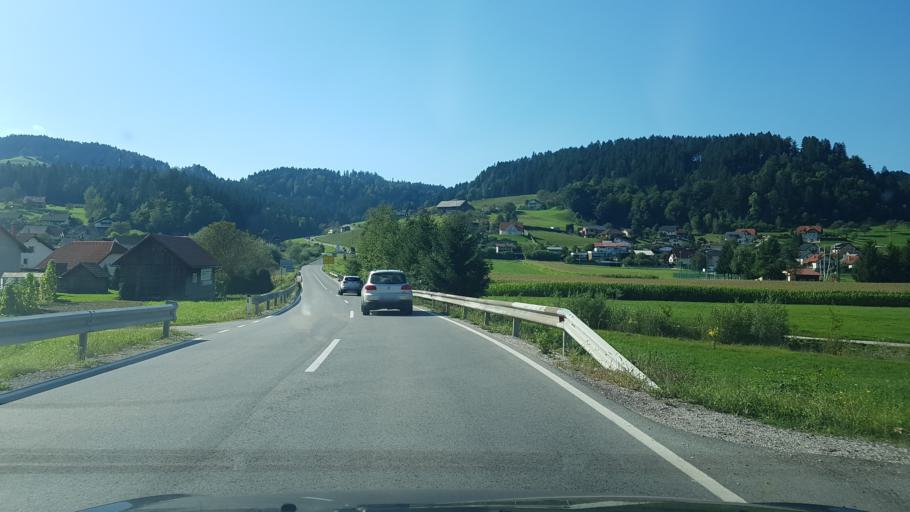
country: SI
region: Slovenj Gradec
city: Slovenj Gradec
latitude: 46.5004
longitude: 15.0713
